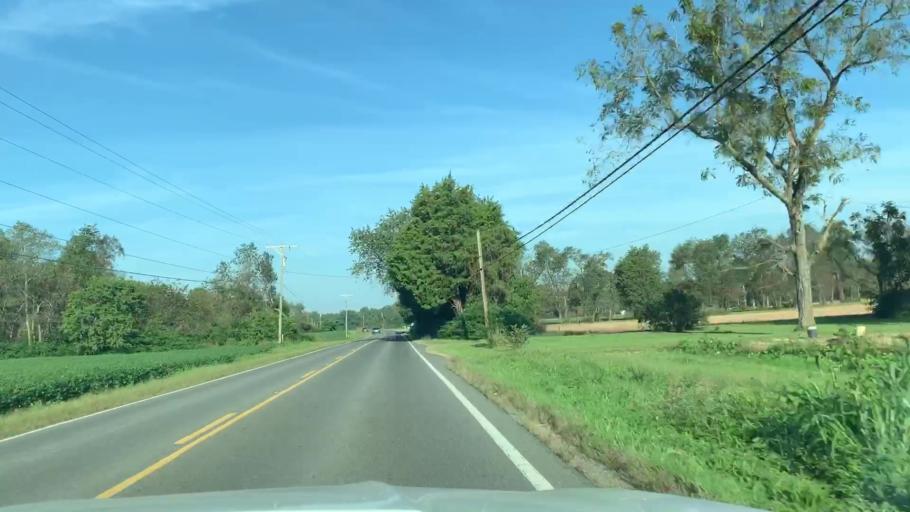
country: US
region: Virginia
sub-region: Lancaster County
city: Lancaster
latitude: 37.7663
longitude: -76.4299
